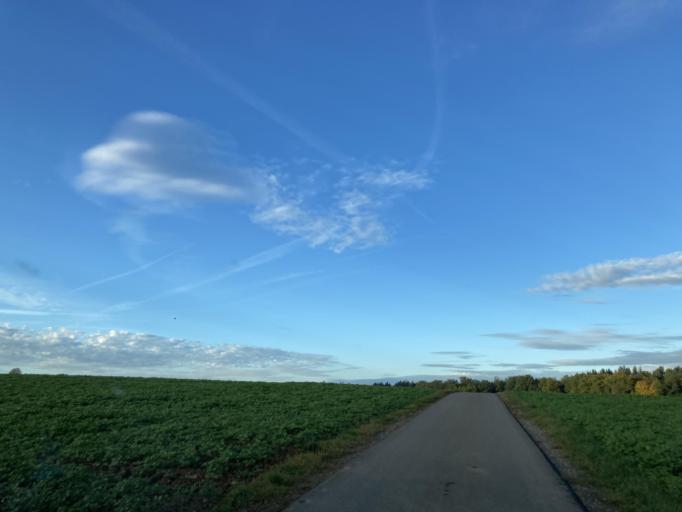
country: DE
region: Baden-Wuerttemberg
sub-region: Regierungsbezirk Stuttgart
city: Motzingen
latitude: 48.5094
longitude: 8.7904
